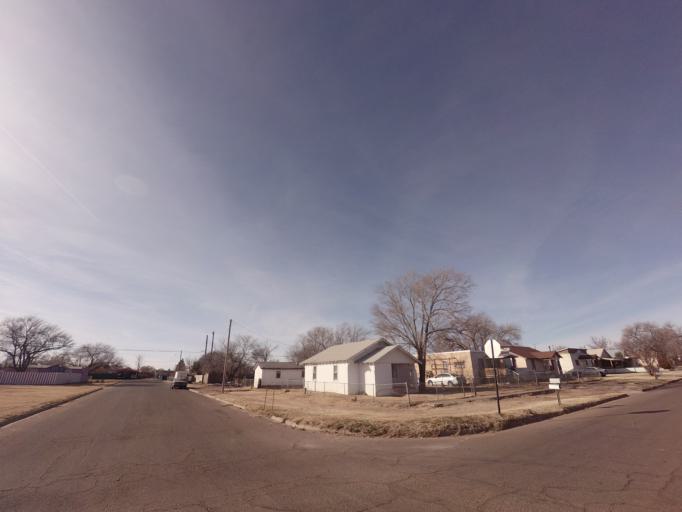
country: US
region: New Mexico
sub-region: Curry County
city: Clovis
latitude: 34.4058
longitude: -103.2217
